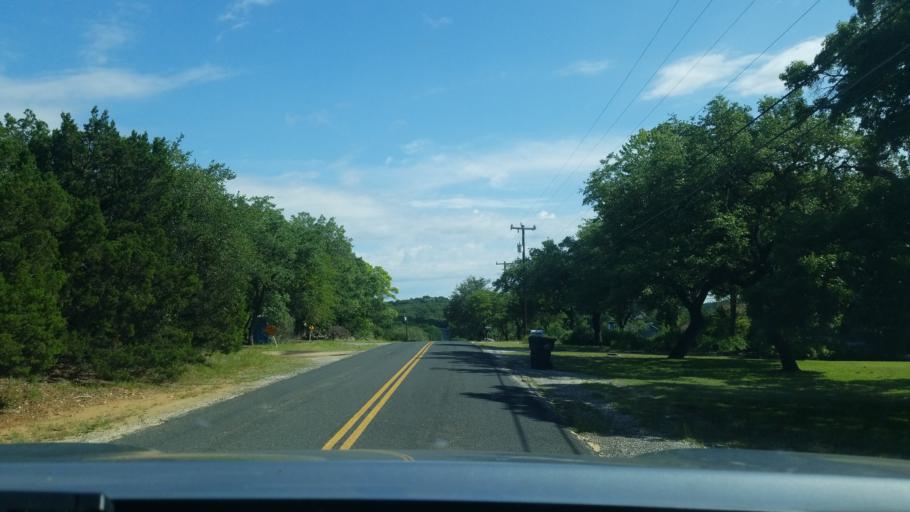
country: US
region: Texas
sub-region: Comal County
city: Bulverde
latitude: 29.7478
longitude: -98.4427
